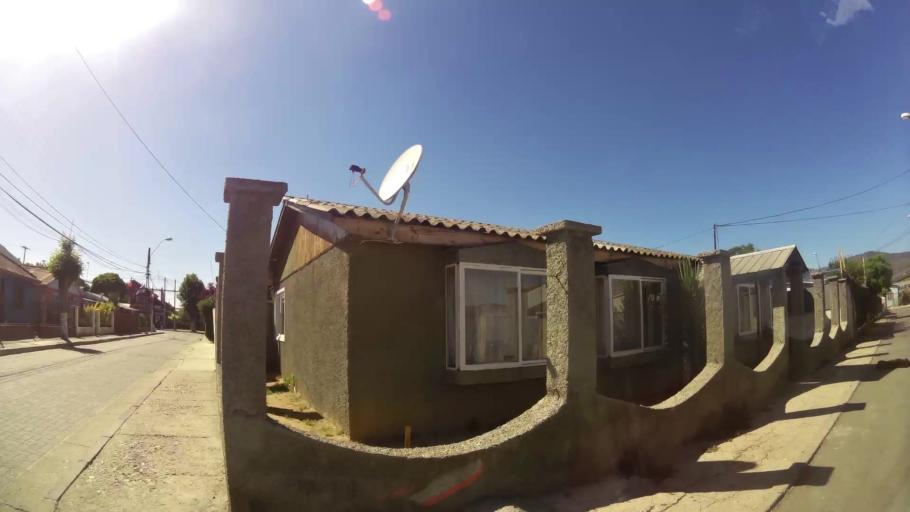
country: CL
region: Valparaiso
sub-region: Provincia de Marga Marga
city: Quilpue
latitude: -33.3234
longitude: -71.4005
